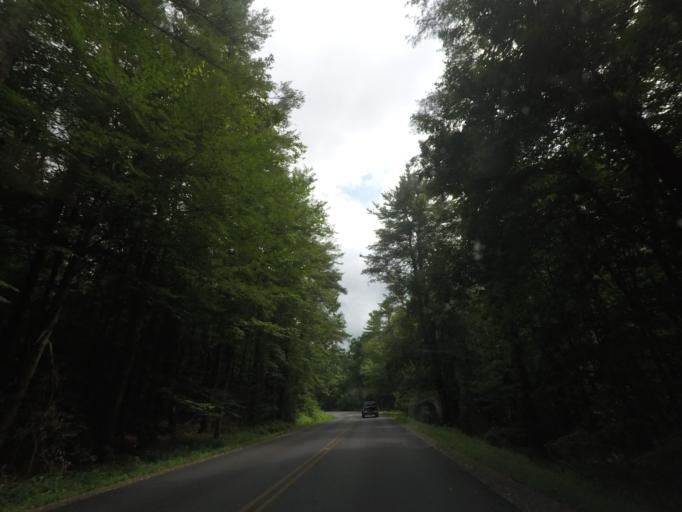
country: US
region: New York
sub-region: Saratoga County
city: Stillwater
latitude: 42.8611
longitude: -73.5562
